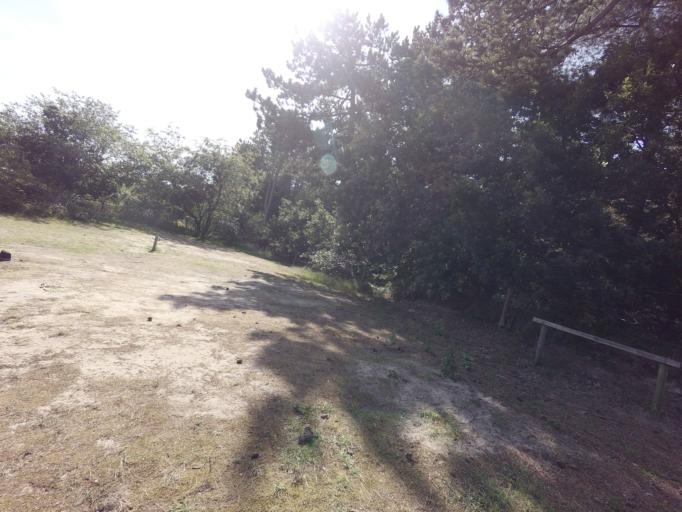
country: NL
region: Friesland
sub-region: Gemeente Ameland
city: Nes
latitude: 53.4542
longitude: 5.7666
